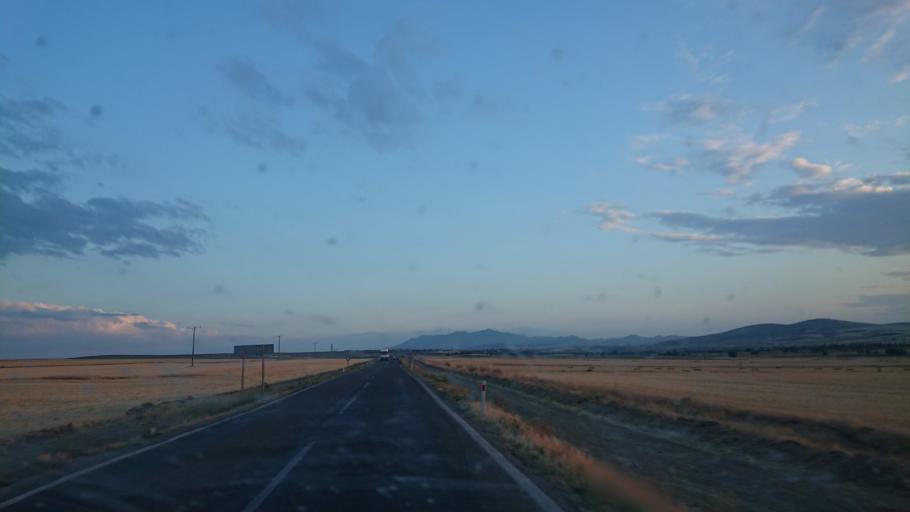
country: TR
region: Aksaray
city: Balci
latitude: 38.8218
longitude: 34.1358
